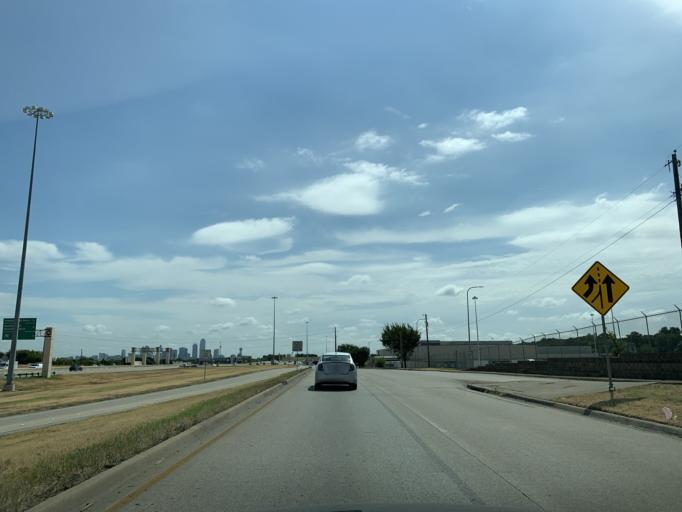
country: US
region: Texas
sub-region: Dallas County
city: Cockrell Hill
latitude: 32.7666
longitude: -96.8700
